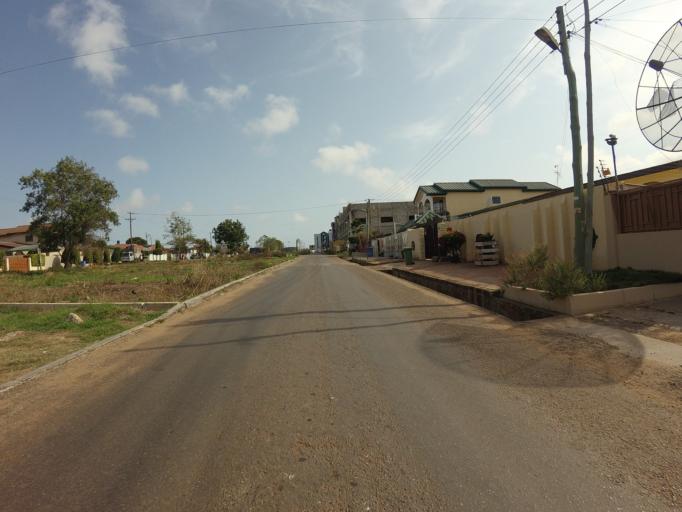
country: GH
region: Greater Accra
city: Nungua
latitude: 5.6379
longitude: -0.1008
